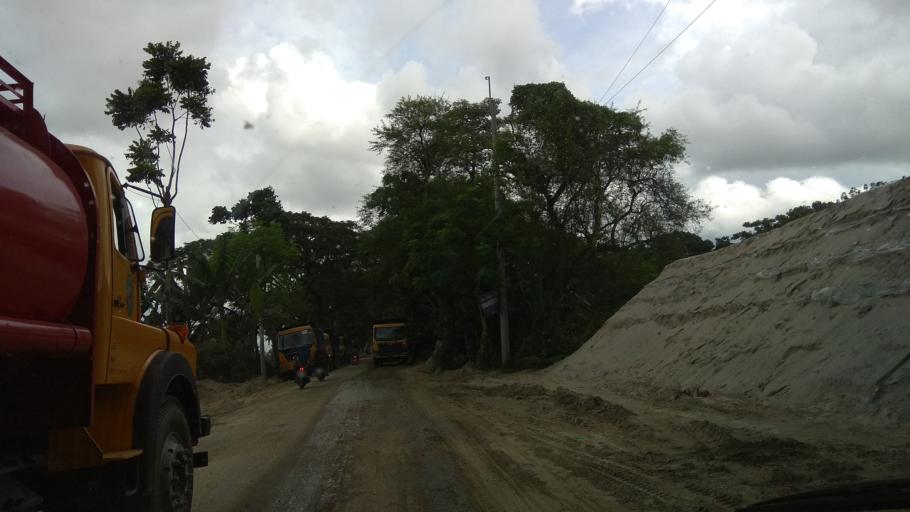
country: BD
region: Khulna
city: Kalia
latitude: 23.1976
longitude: 89.6968
